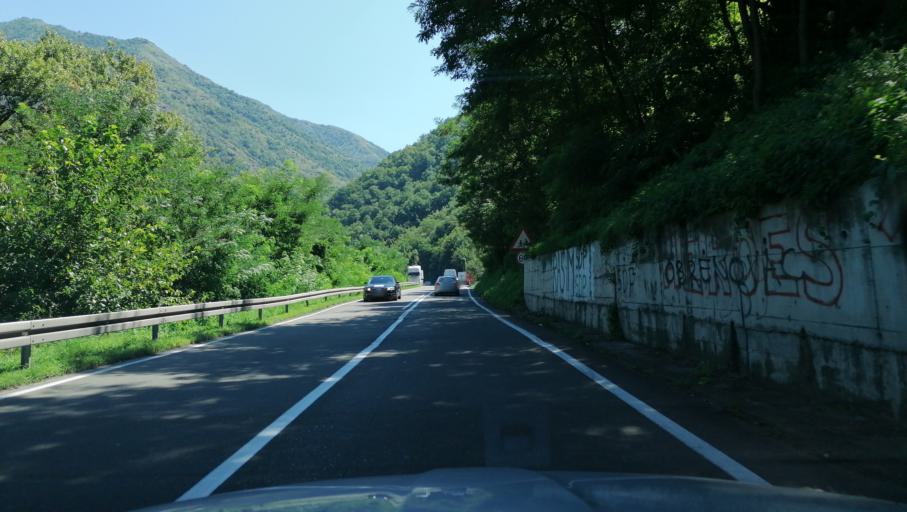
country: RS
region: Central Serbia
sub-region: Raski Okrug
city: Kraljevo
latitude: 43.6122
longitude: 20.5478
